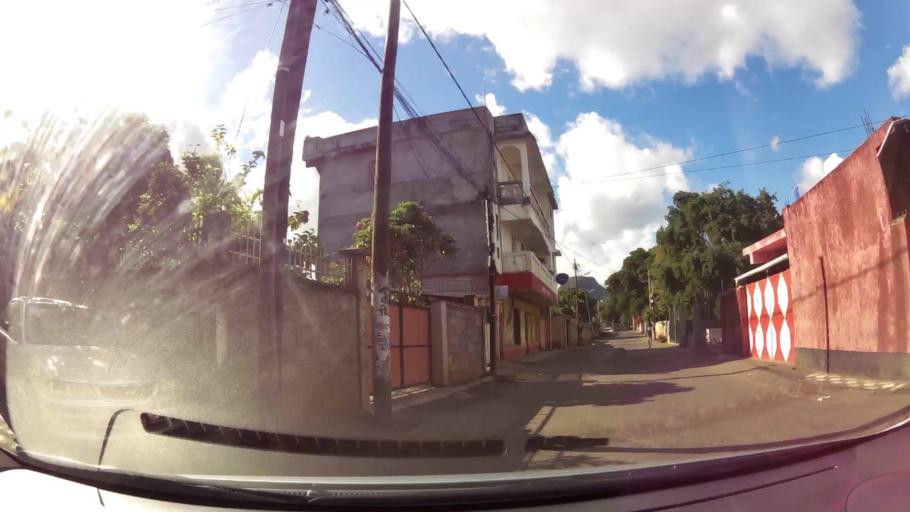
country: MU
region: Pamplemousses
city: Le Hochet
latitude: -20.1473
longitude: 57.5133
